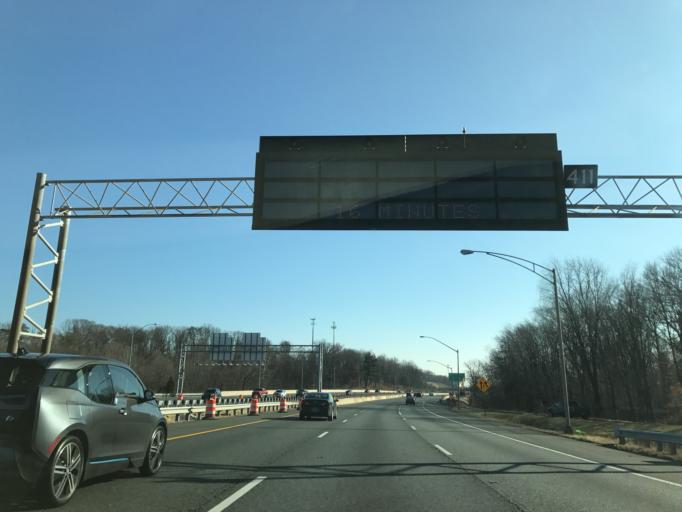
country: US
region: Maryland
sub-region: Baltimore County
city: Overlea
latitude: 39.3678
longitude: -76.5111
